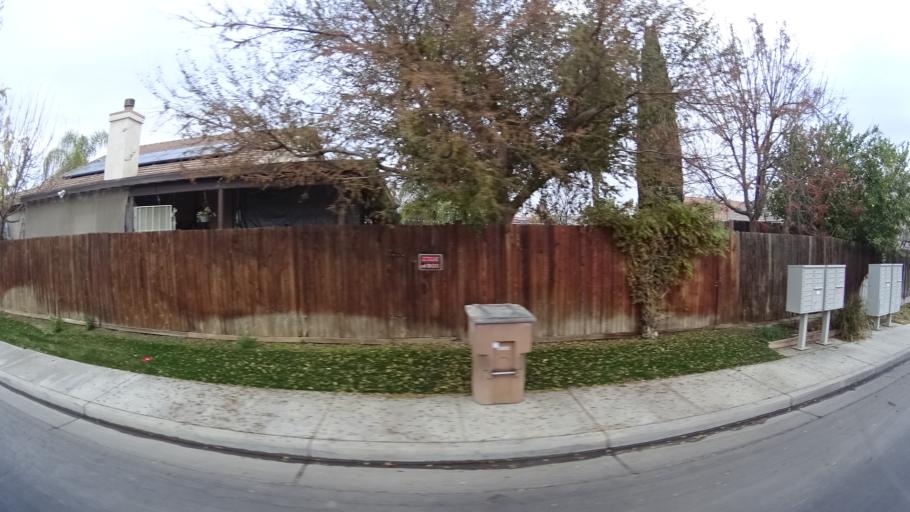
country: US
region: California
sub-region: Kern County
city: Greenfield
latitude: 35.3004
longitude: -119.0805
